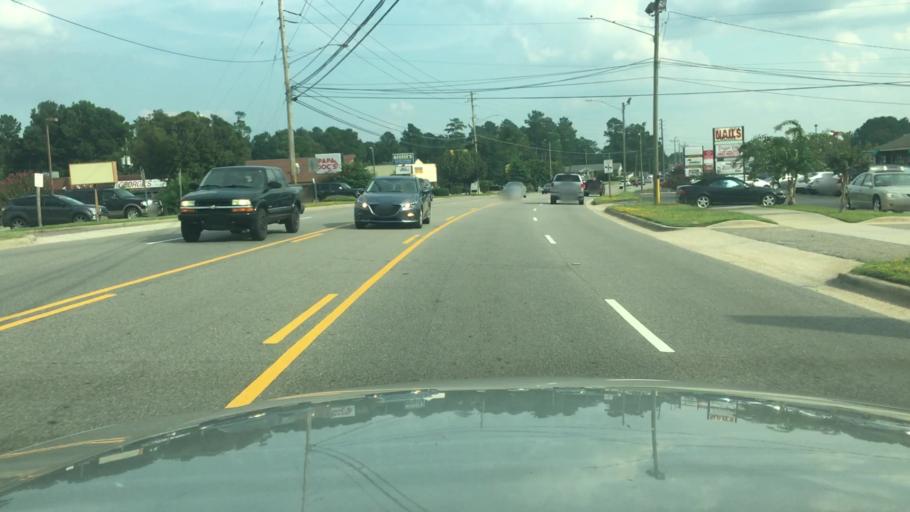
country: US
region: North Carolina
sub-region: Cumberland County
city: Fort Bragg
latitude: 35.1010
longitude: -78.9905
